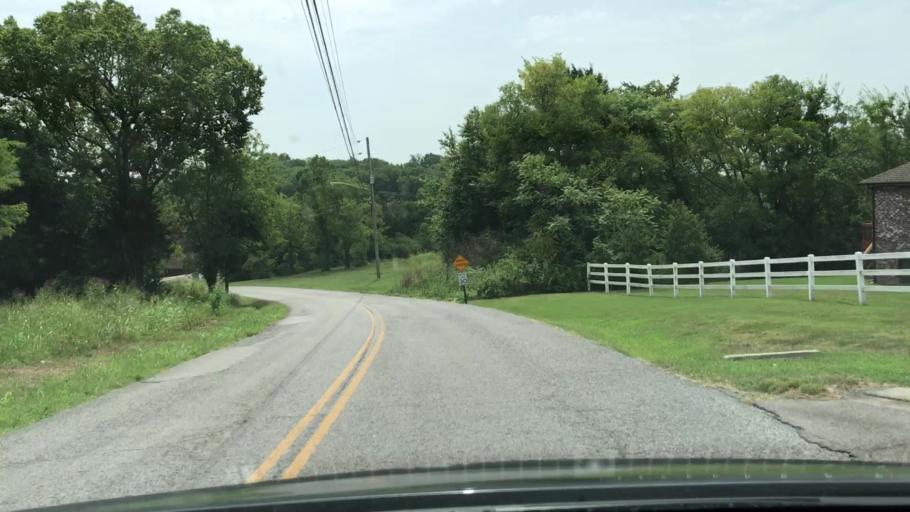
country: US
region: Tennessee
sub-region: Rutherford County
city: La Vergne
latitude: 35.9729
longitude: -86.5889
